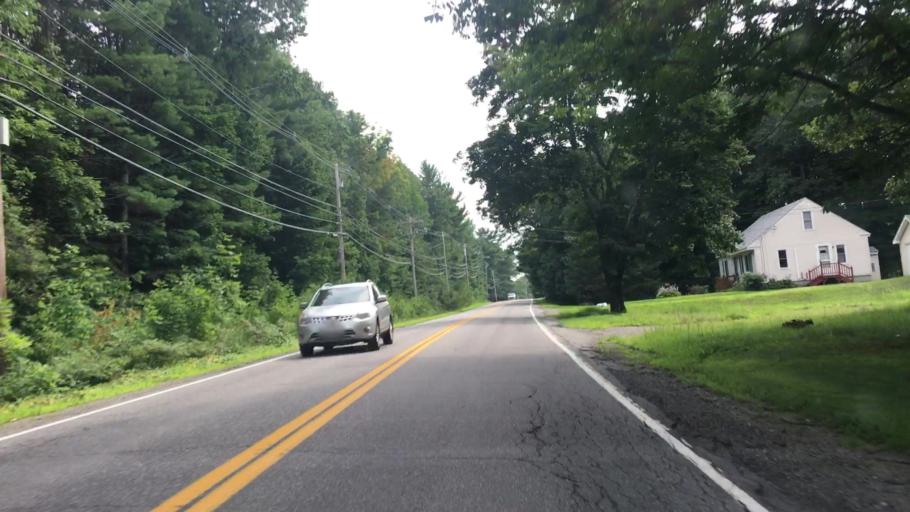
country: US
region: Maine
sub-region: Kennebec County
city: Winslow
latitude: 44.5202
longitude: -69.6308
